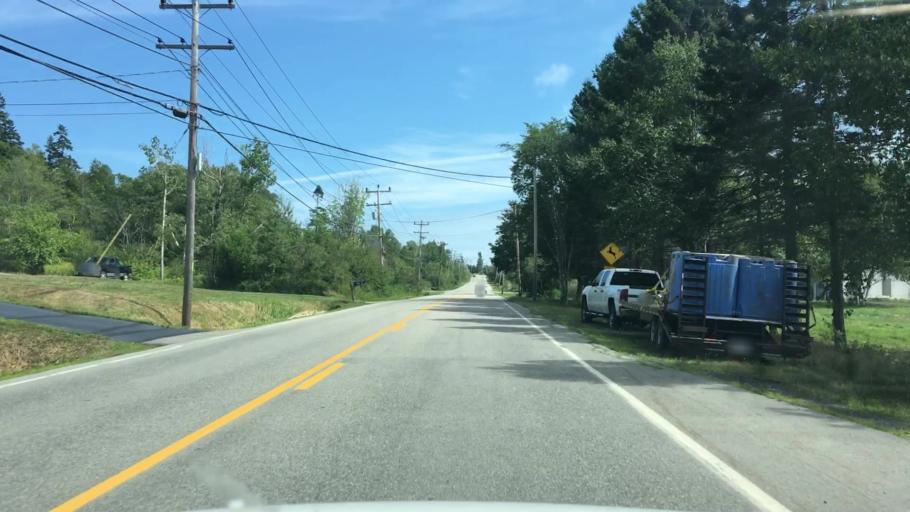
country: US
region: Maine
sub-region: Washington County
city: Eastport
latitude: 44.9186
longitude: -67.0139
